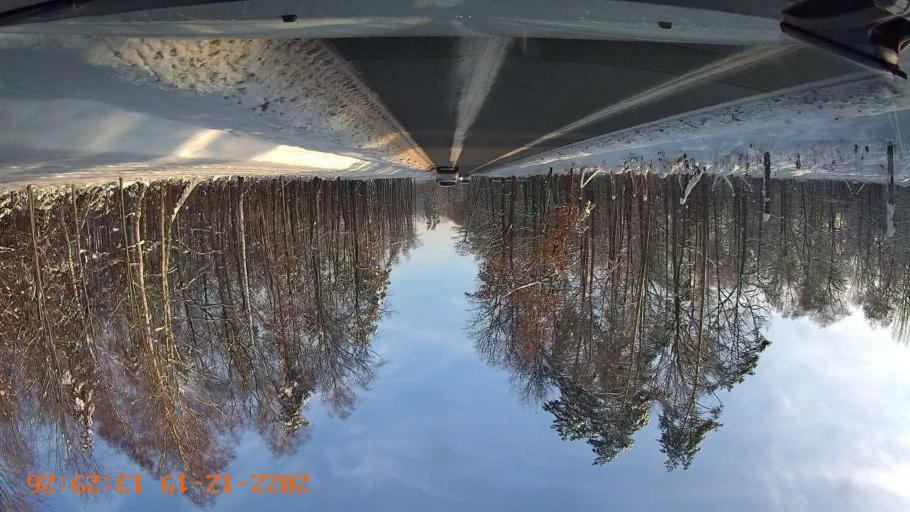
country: PL
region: Silesian Voivodeship
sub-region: Powiat bierunsko-ledzinski
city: Ledziny
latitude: 50.1146
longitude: 19.1190
